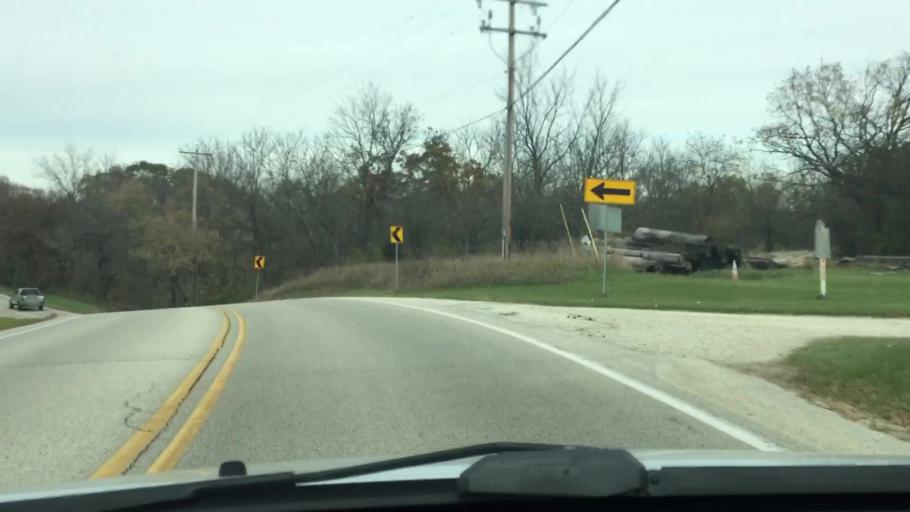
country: US
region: Wisconsin
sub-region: Waukesha County
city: North Prairie
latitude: 42.9050
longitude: -88.4051
